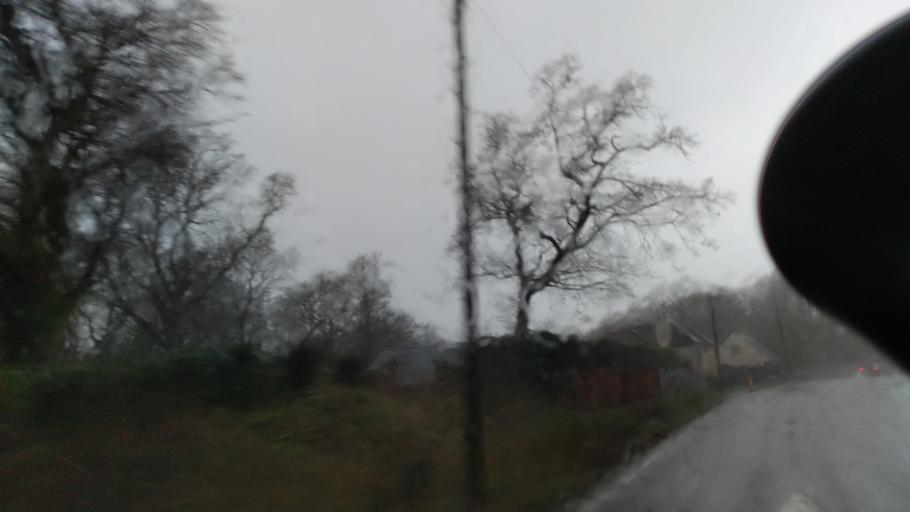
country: GB
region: England
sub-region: West Sussex
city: Arundel
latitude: 50.8553
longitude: -0.5772
